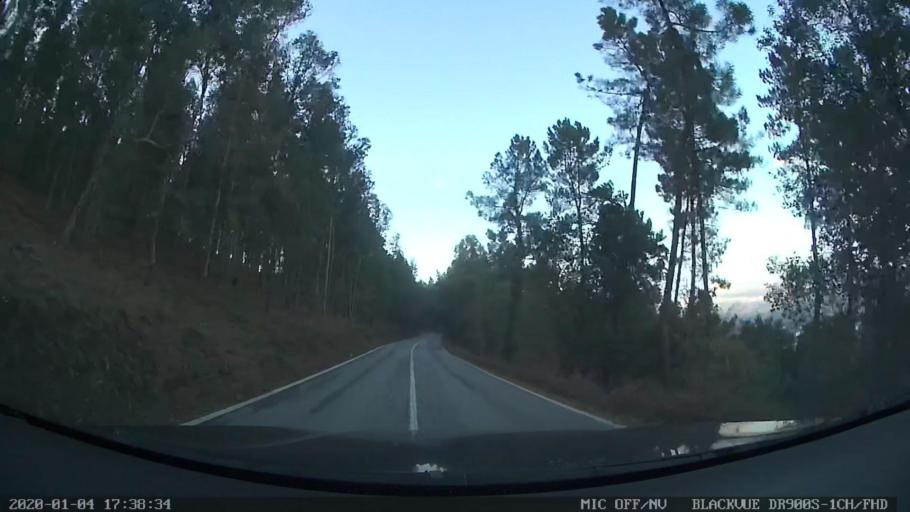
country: PT
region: Vila Real
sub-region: Mondim de Basto
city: Mondim de Basto
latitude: 41.4555
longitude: -7.9596
